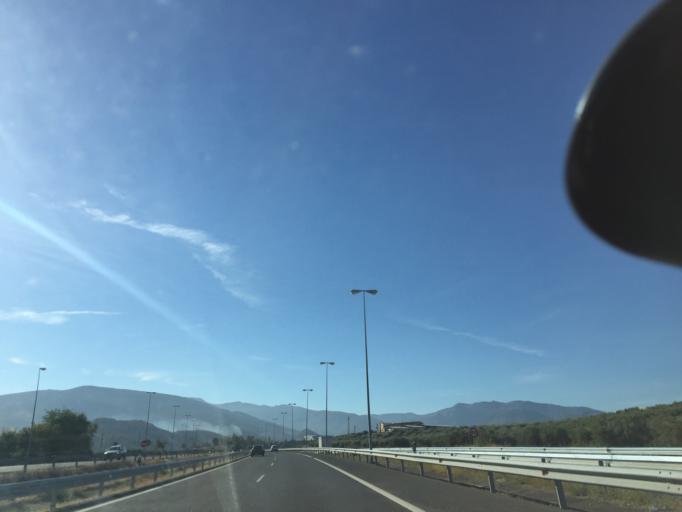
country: ES
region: Andalusia
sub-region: Provincia de Jaen
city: Jaen
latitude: 37.7896
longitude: -3.7577
